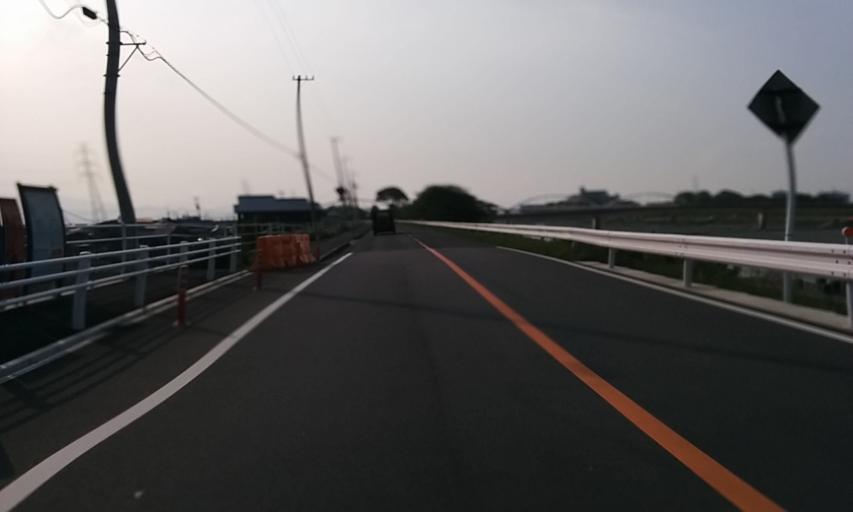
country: JP
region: Ehime
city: Saijo
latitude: 33.8982
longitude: 133.1912
